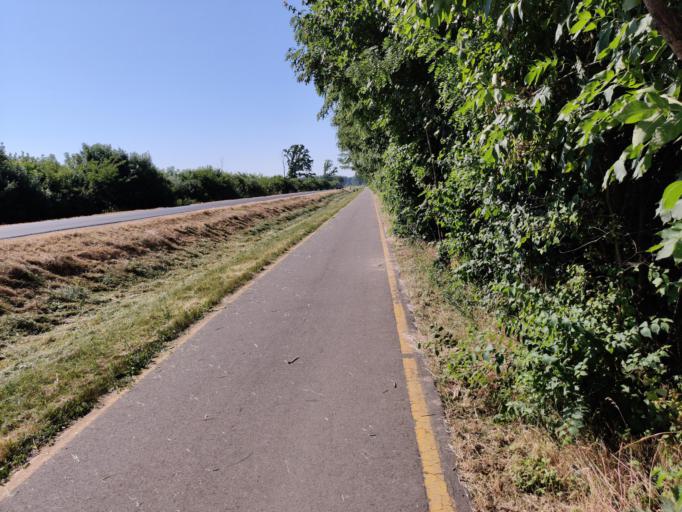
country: HU
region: Hajdu-Bihar
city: Balmazujvaros
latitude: 47.5956
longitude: 21.3397
